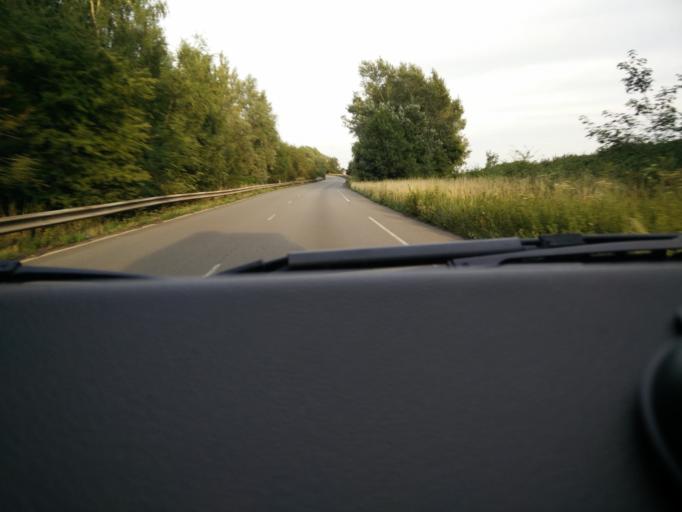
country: FR
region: Nord-Pas-de-Calais
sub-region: Departement du Nord
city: Marly
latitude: 50.3353
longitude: 3.5494
